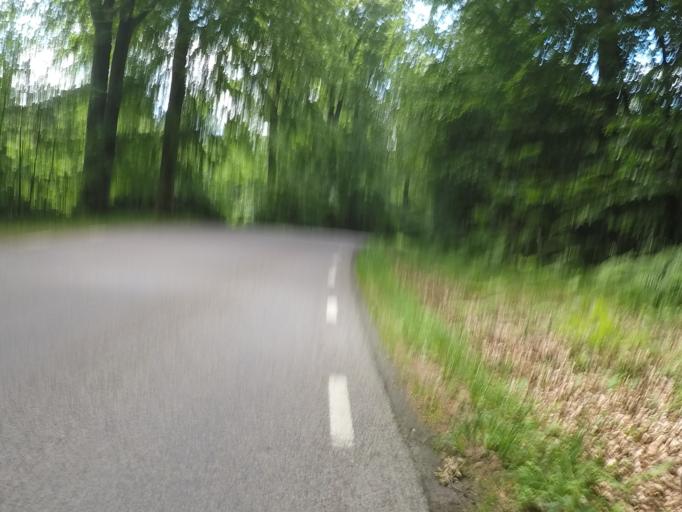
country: SE
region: Skane
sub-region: Svedala Kommun
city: Klagerup
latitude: 55.5552
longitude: 13.2101
